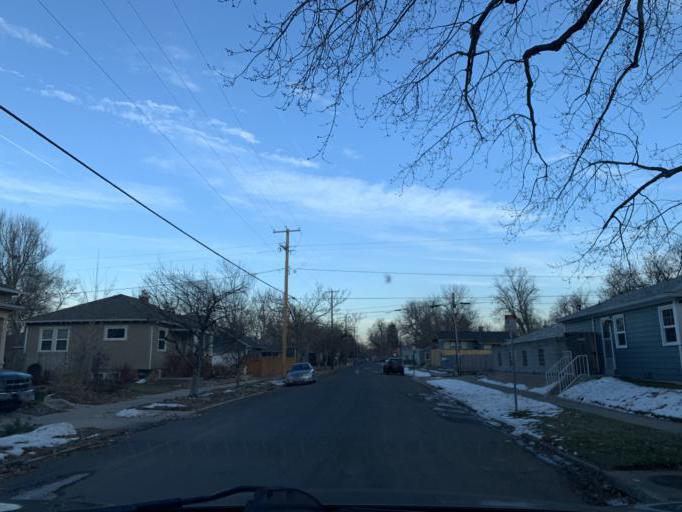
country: US
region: Colorado
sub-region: Adams County
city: Berkley
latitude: 39.7783
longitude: -105.0375
